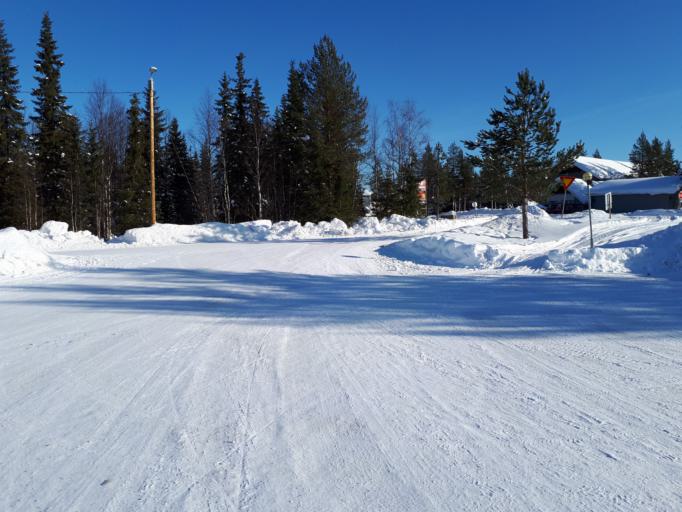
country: FI
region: Lapland
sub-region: Tunturi-Lappi
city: Kolari
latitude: 67.6004
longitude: 24.1520
